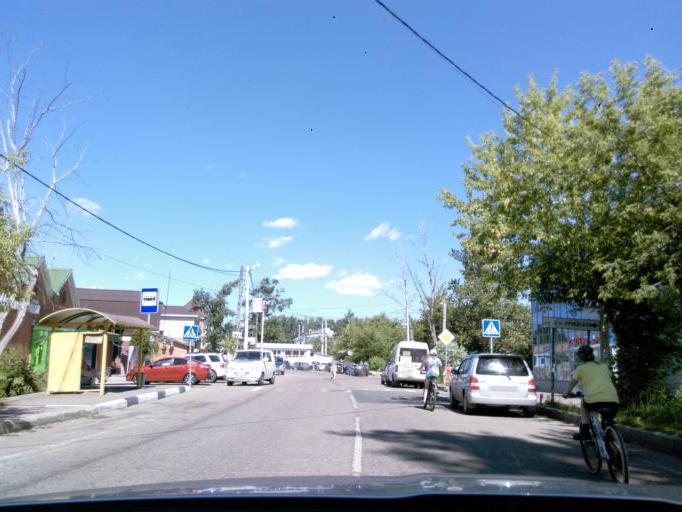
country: RU
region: Moskovskaya
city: Solnechnogorsk
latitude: 56.1837
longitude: 36.9693
